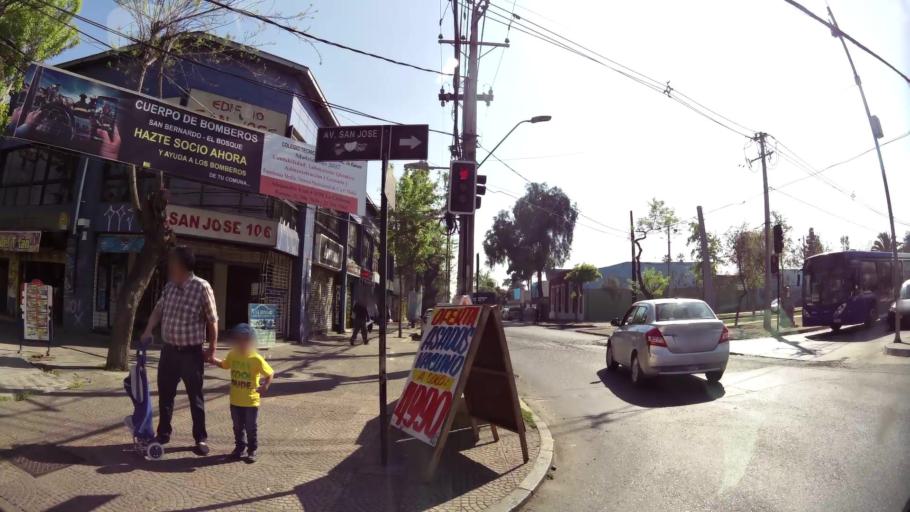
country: CL
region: Santiago Metropolitan
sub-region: Provincia de Maipo
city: San Bernardo
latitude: -33.5971
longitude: -70.6999
